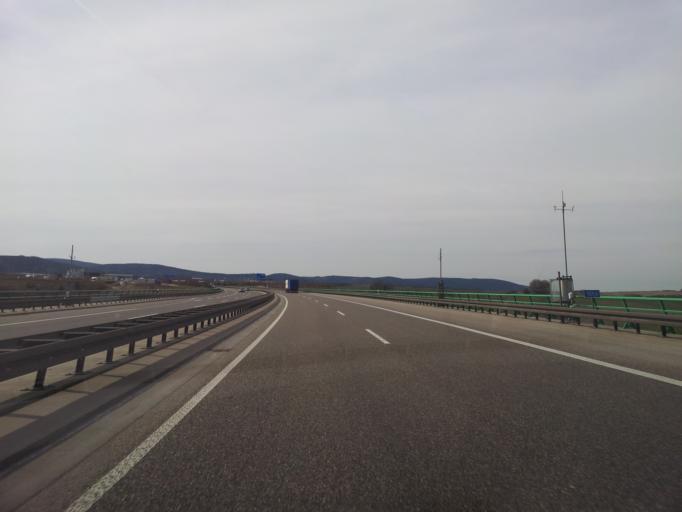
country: DE
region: Thuringia
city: Geraberg
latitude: 50.7255
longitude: 10.8543
